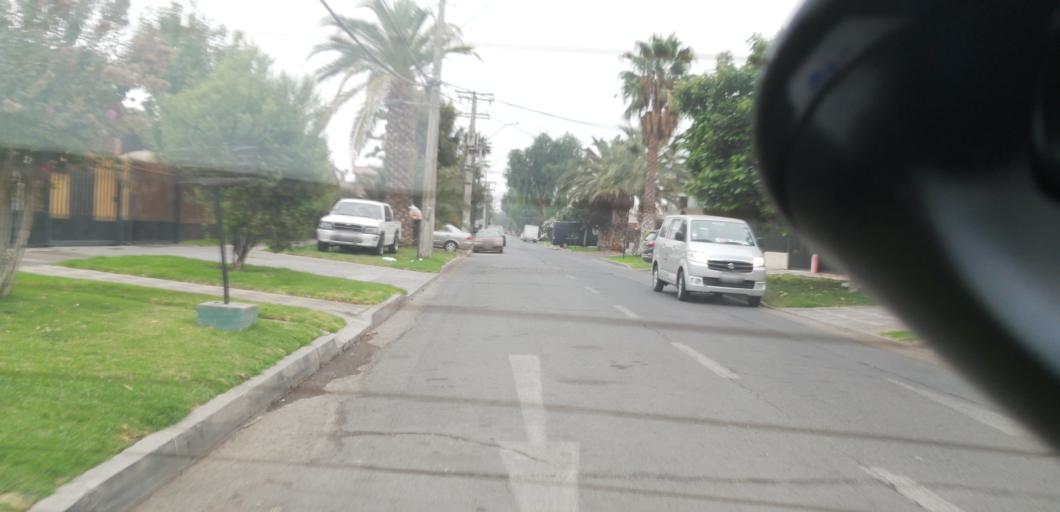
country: CL
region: Santiago Metropolitan
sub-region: Provincia de Santiago
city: Lo Prado
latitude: -33.4539
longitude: -70.7679
